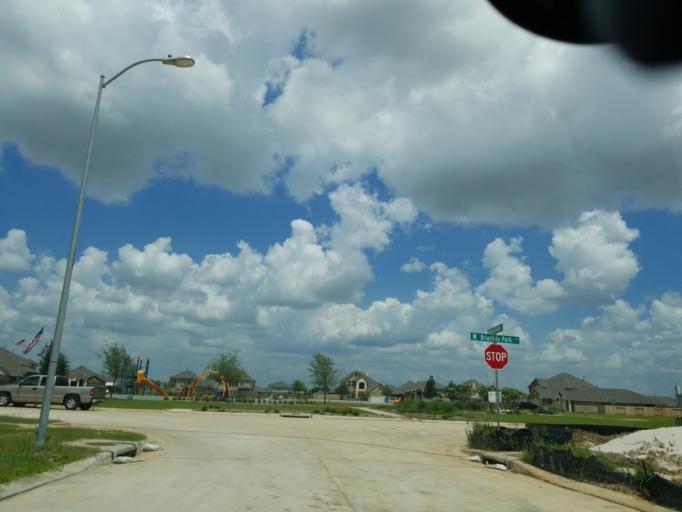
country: US
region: Texas
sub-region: Harris County
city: Katy
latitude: 29.8288
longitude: -95.7794
